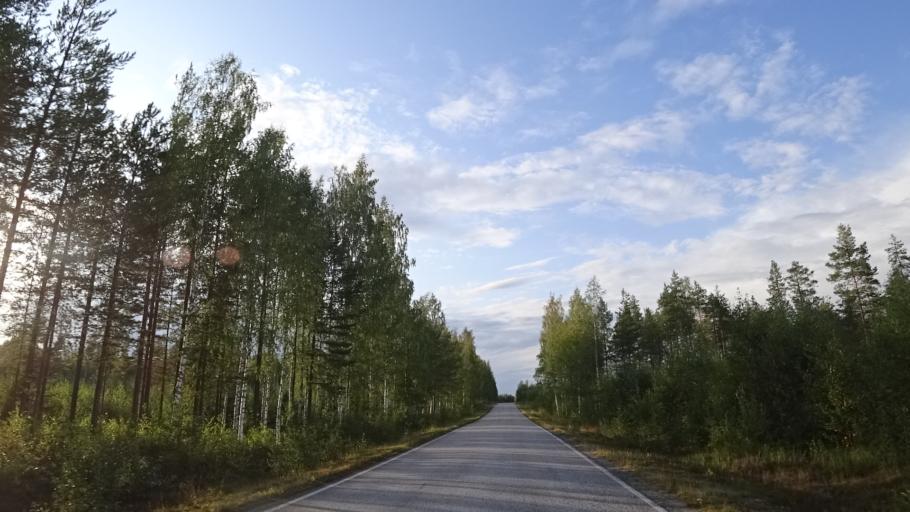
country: FI
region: North Karelia
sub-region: Pielisen Karjala
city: Lieksa
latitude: 63.3521
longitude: 30.2650
